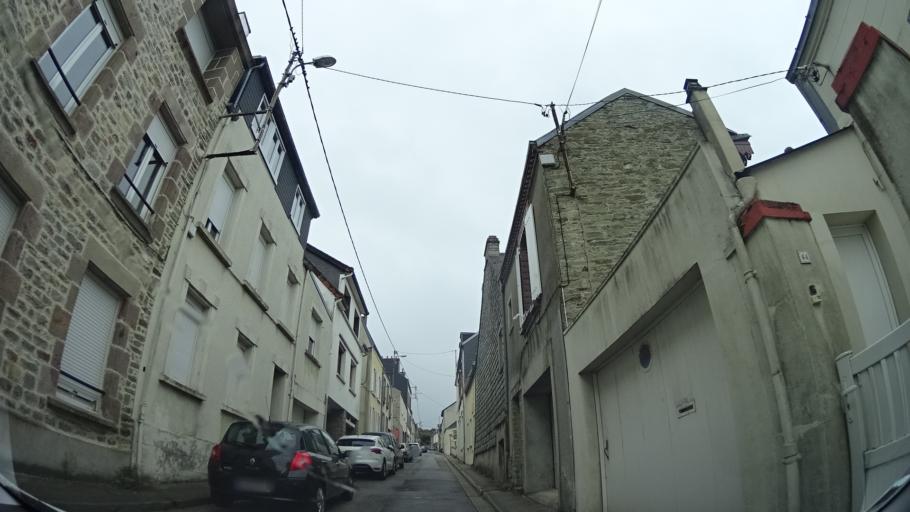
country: FR
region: Lower Normandy
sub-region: Departement de la Manche
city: Cherbourg-Octeville
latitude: 49.6323
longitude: -1.6260
